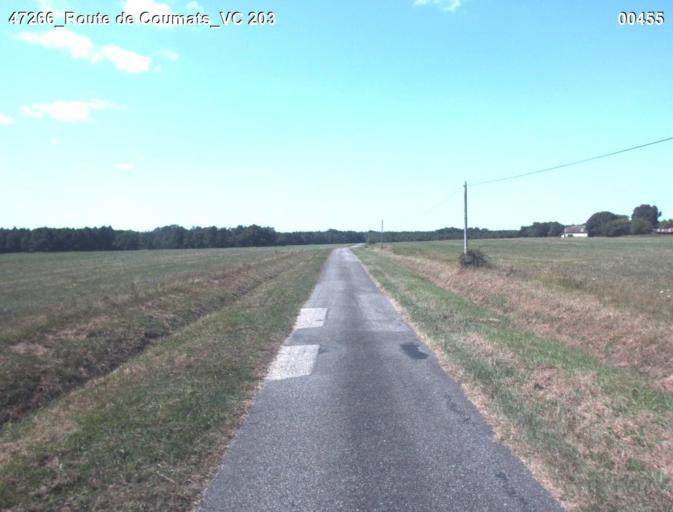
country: FR
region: Aquitaine
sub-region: Departement des Landes
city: Gabarret
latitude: 44.0137
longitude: 0.0902
